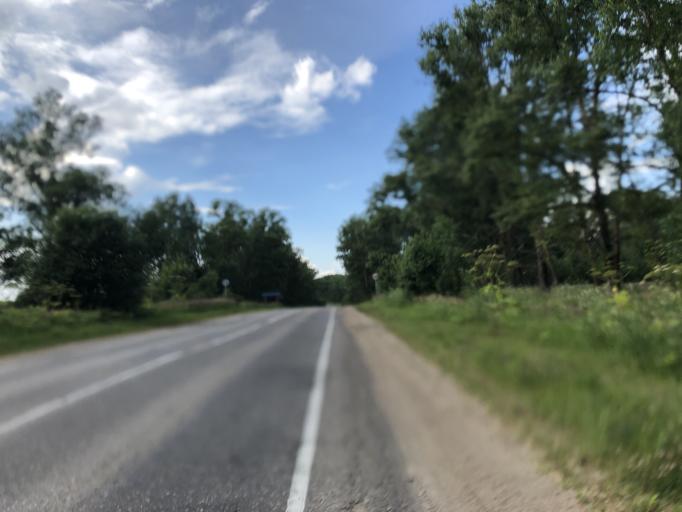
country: RU
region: Tverskaya
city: Rzhev
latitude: 56.2647
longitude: 34.2515
